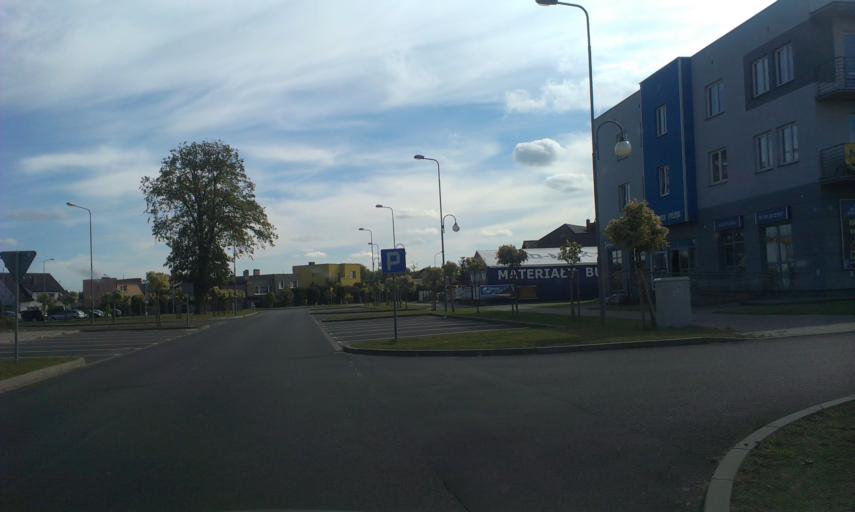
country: PL
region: Greater Poland Voivodeship
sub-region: Powiat zlotowski
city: Zlotow
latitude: 53.3728
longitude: 17.0206
